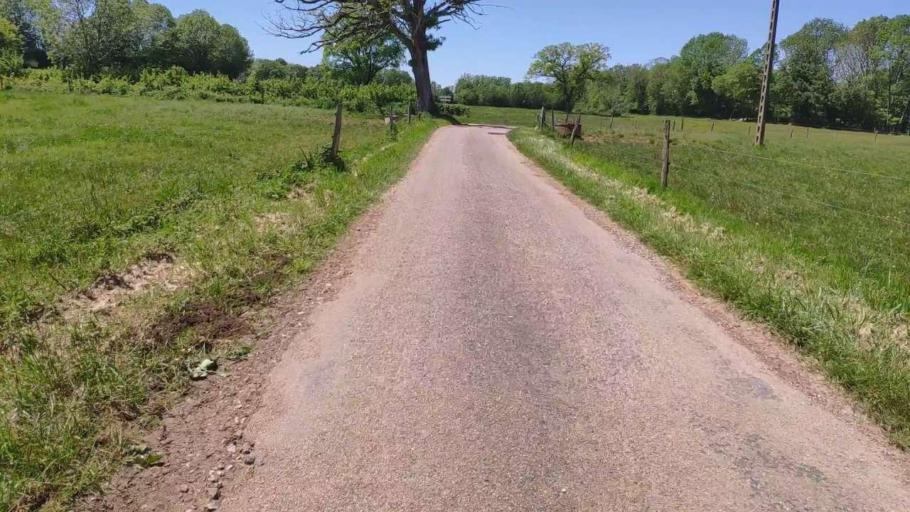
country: FR
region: Franche-Comte
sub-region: Departement du Jura
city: Poligny
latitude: 46.7516
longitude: 5.6847
